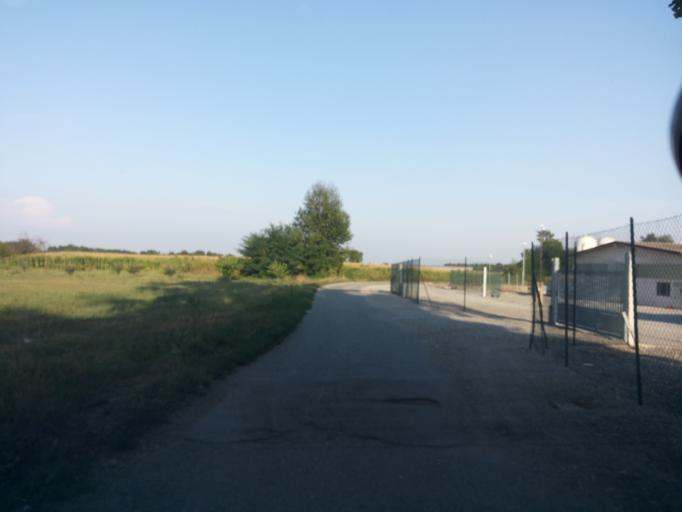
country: IT
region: Piedmont
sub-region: Provincia di Biella
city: Cavaglia
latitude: 45.3943
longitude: 8.1149
